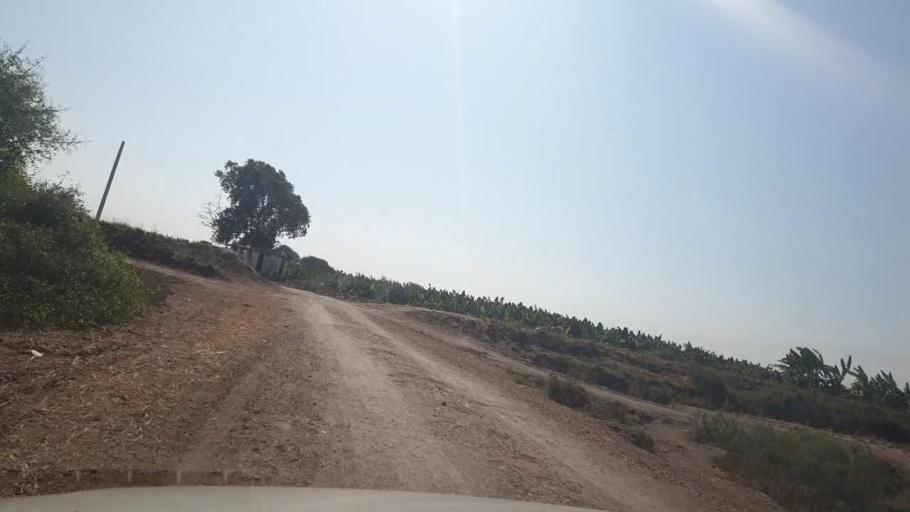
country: PK
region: Sindh
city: Chuhar Jamali
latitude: 24.4510
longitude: 67.8632
